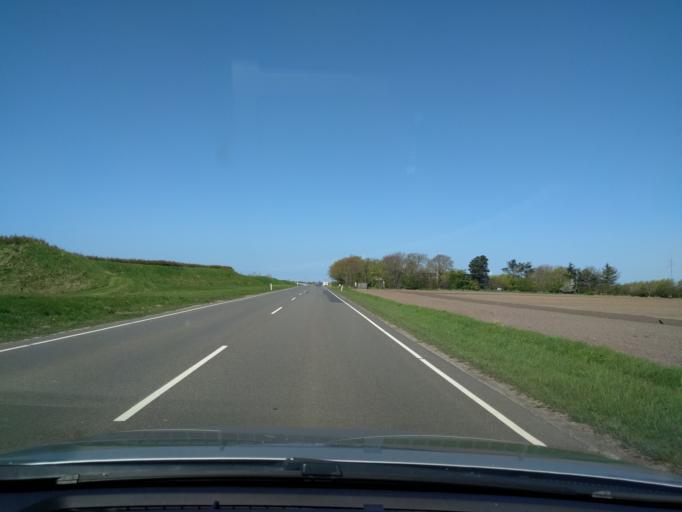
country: DK
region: Central Jutland
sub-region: Ringkobing-Skjern Kommune
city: Ringkobing
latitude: 56.1036
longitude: 8.2666
